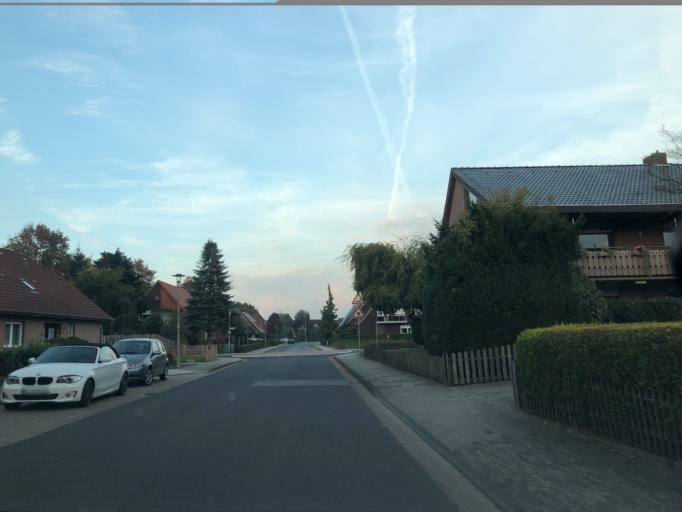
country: DE
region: Lower Saxony
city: Papenburg
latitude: 53.0738
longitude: 7.4358
